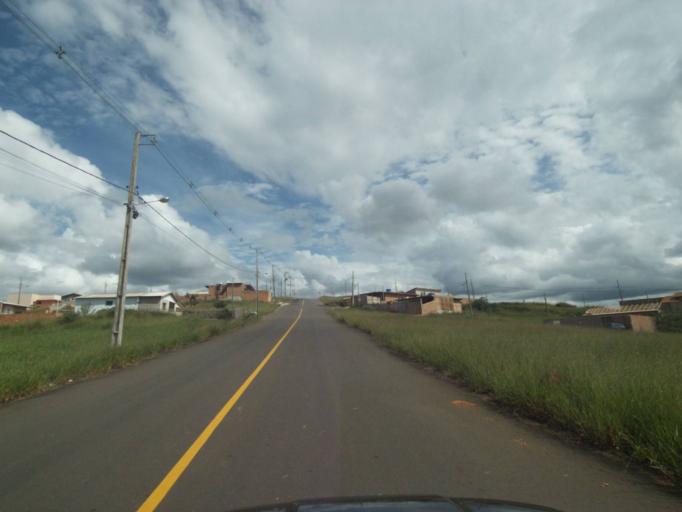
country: BR
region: Parana
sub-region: Telemaco Borba
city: Telemaco Borba
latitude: -24.3084
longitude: -50.6401
